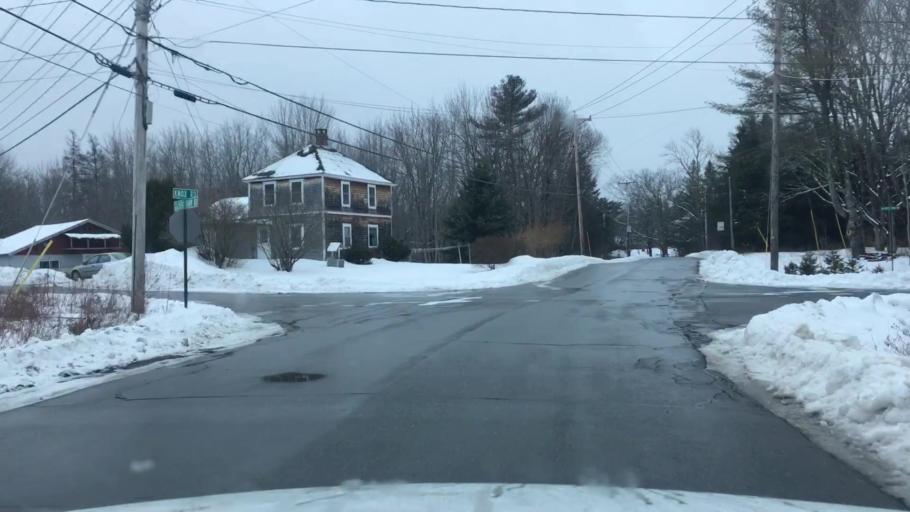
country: US
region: Maine
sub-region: Hancock County
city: Trenton
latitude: 44.4114
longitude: -68.3344
